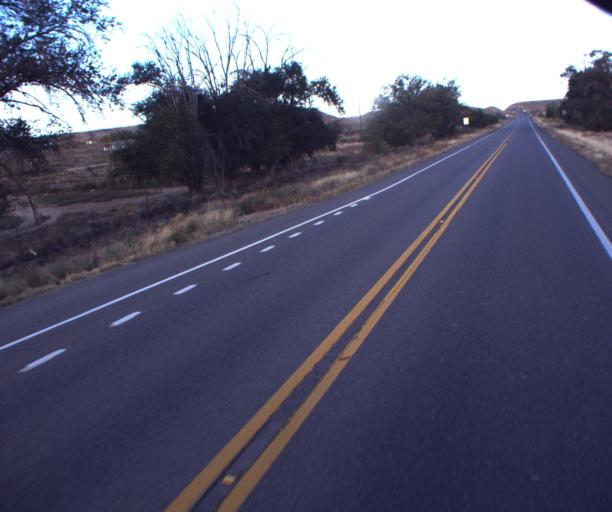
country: US
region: New Mexico
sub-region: San Juan County
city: Shiprock
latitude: 36.9308
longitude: -109.1050
